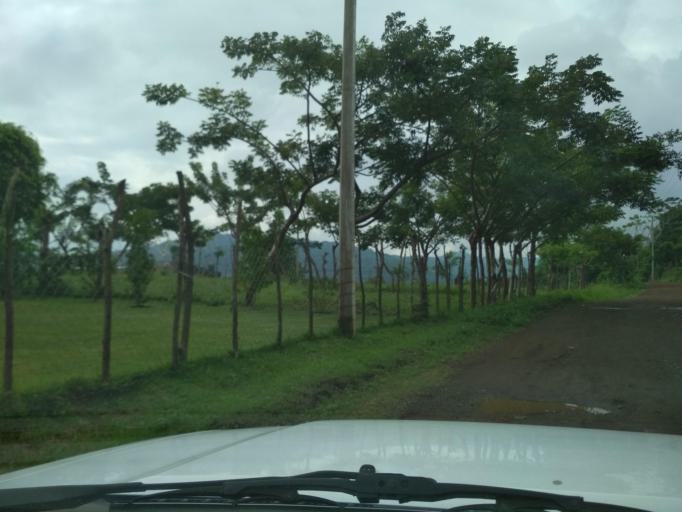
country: MX
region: Veracruz
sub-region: San Andres Tuxtla
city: Matacapan
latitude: 18.4391
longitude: -95.1497
